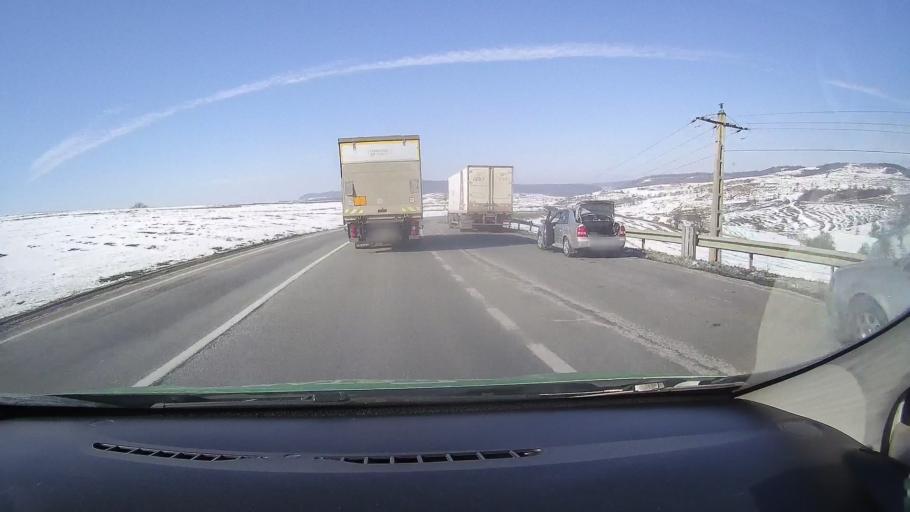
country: RO
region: Brasov
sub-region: Oras Rupea
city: Fiser
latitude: 46.0899
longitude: 25.1191
